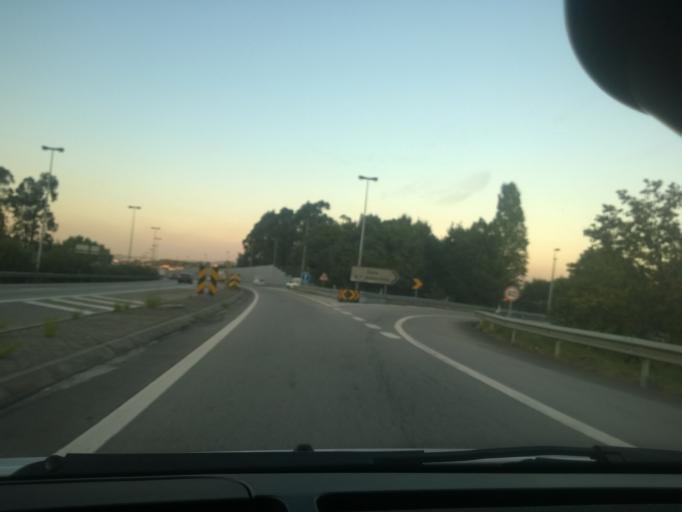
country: PT
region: Porto
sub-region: Vila Nova de Gaia
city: Avintes
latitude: 41.1023
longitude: -8.5675
